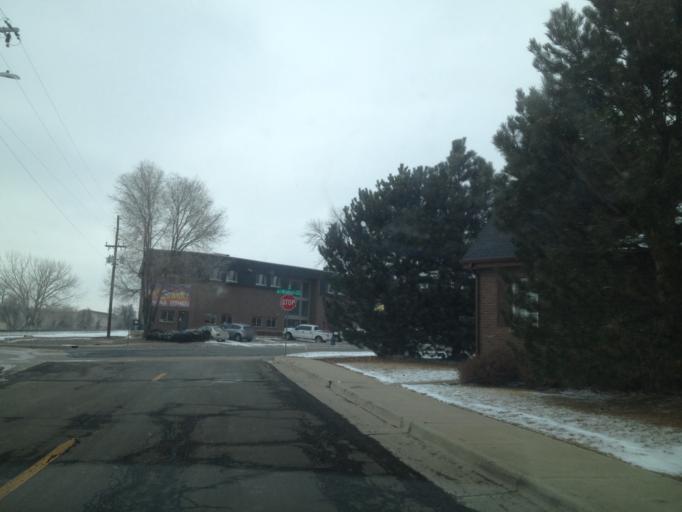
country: US
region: Colorado
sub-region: Adams County
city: Westminster
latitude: 39.8285
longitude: -105.0402
